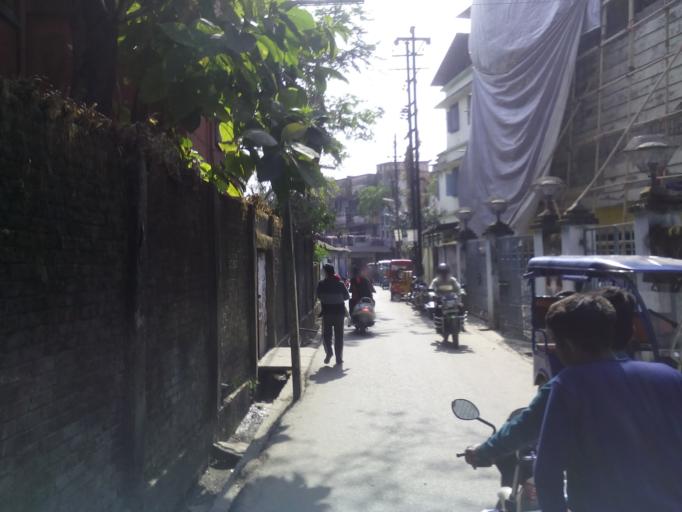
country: IN
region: West Bengal
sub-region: Darjiling
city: Shiliguri
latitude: 26.7094
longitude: 88.4304
